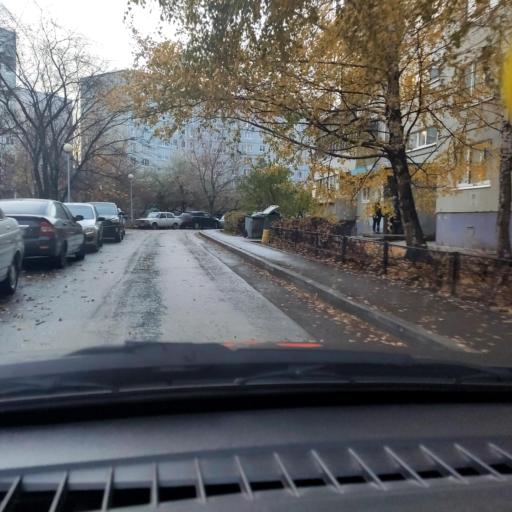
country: RU
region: Samara
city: Tol'yatti
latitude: 53.5456
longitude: 49.3402
